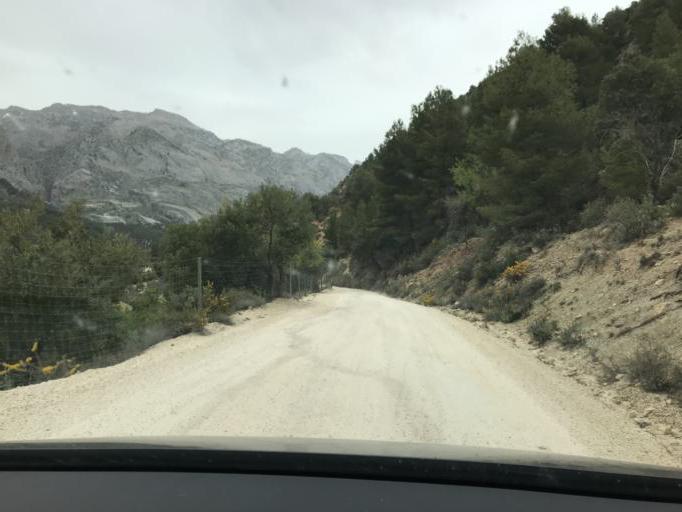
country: ES
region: Andalusia
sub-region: Provincia de Granada
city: Castril
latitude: 37.8281
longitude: -2.7727
